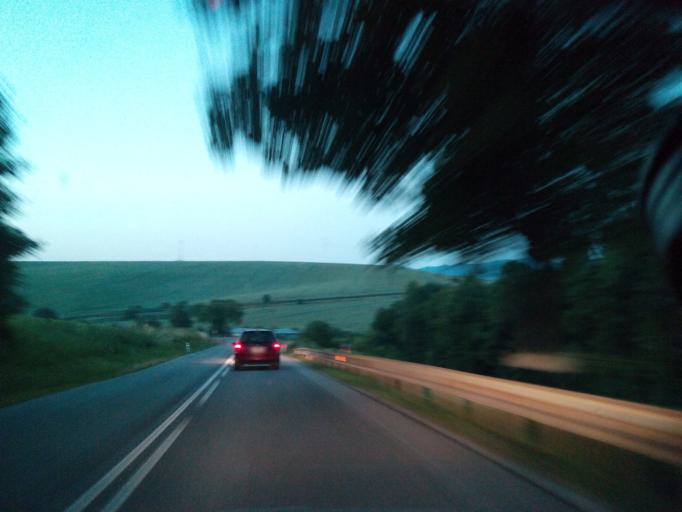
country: SK
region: Presovsky
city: Spisske Podhradie
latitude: 48.9451
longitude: 20.7333
